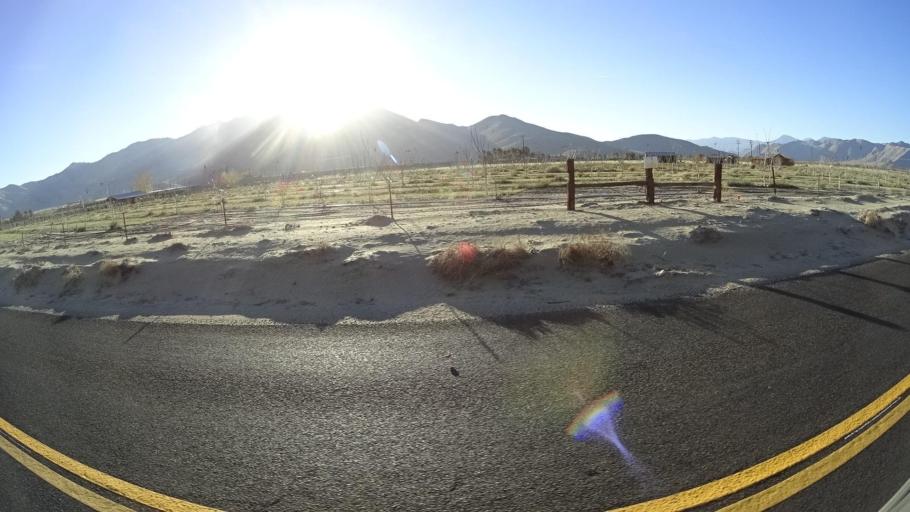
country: US
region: California
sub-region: Kern County
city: Weldon
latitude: 35.6507
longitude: -118.2527
